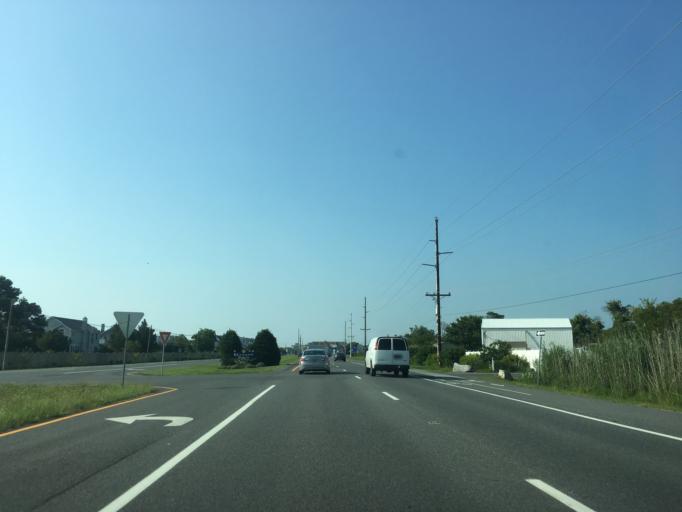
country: US
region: Delaware
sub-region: Sussex County
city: Bethany Beach
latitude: 38.5507
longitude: -75.0594
